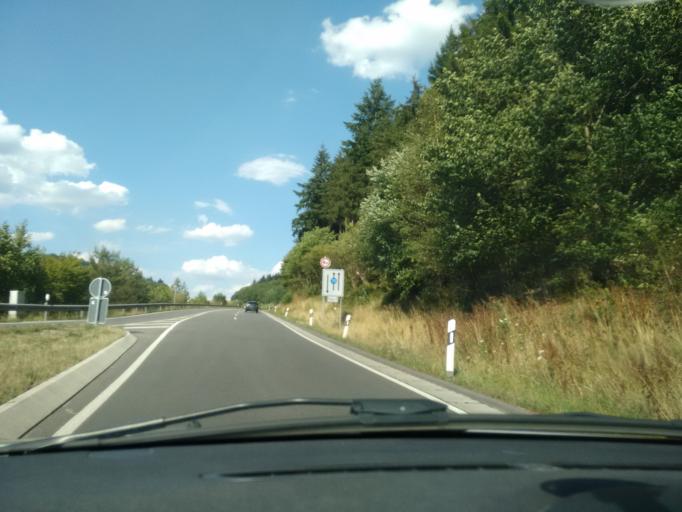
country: DE
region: Rheinland-Pfalz
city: Niederbrombach
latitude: 49.6906
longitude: 7.2497
